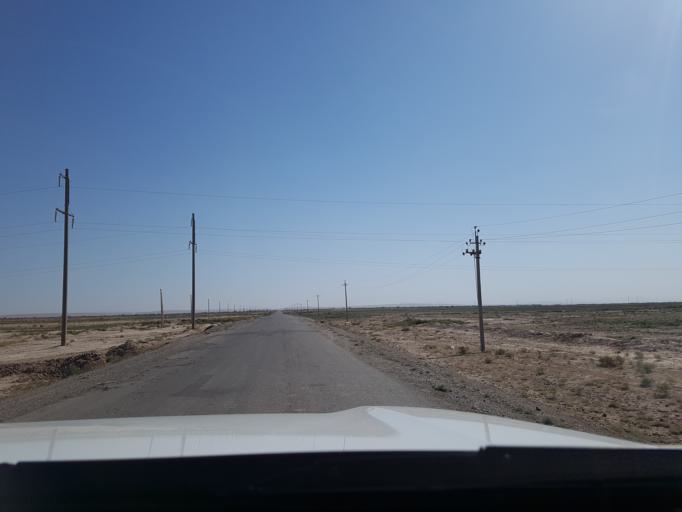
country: IR
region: Razavi Khorasan
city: Sarakhs
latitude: 36.5102
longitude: 61.2532
